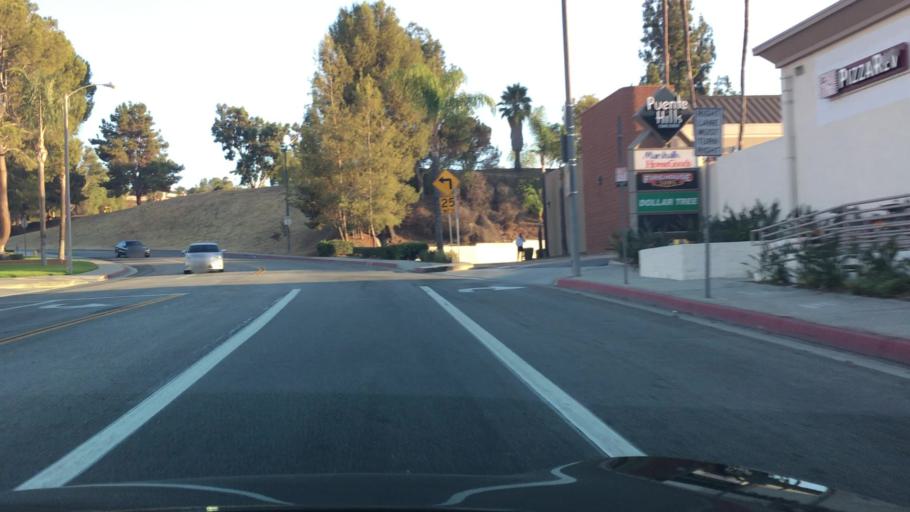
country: US
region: California
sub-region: Los Angeles County
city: Rowland Heights
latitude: 33.9902
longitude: -117.9245
